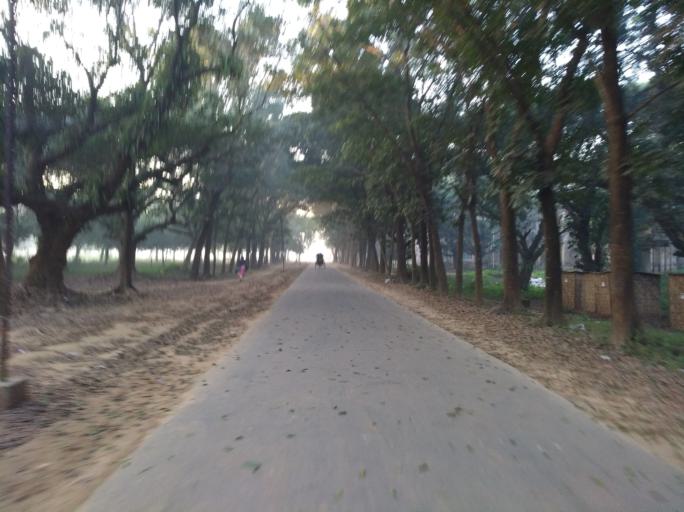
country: BD
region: Dhaka
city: Tungi
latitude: 23.8814
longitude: 90.2713
